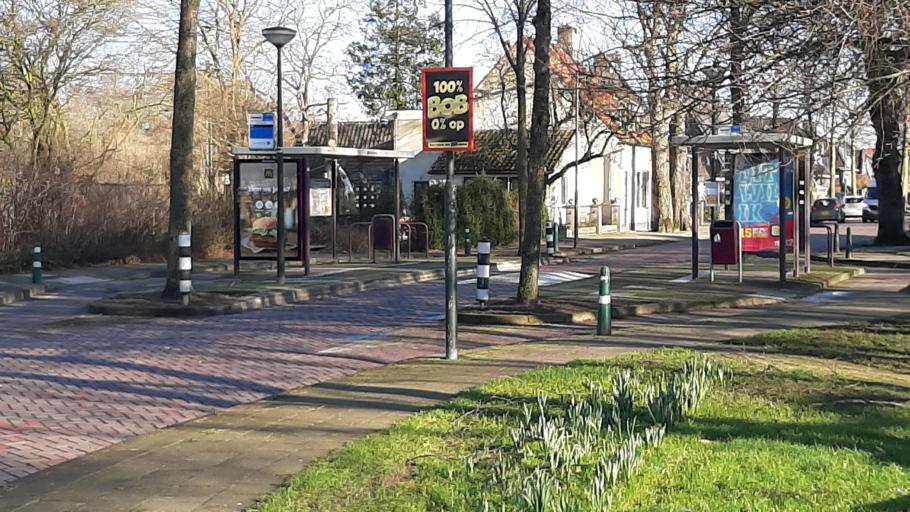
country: NL
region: North Brabant
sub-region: Gemeente Oisterwijk
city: Oisterwijk
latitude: 51.5767
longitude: 5.1709
